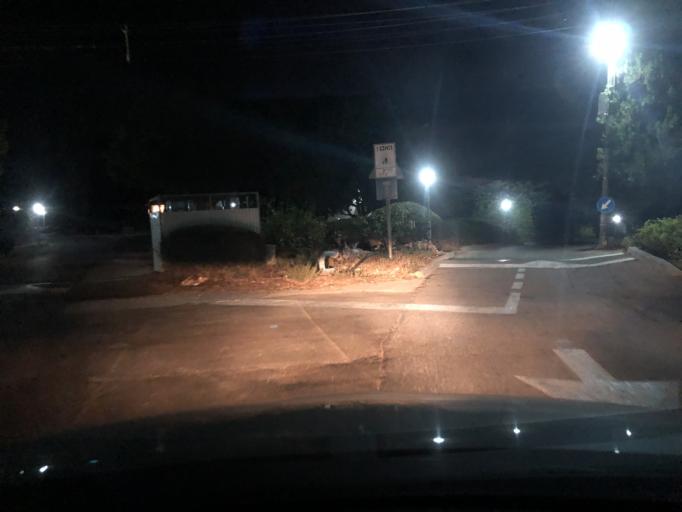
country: IL
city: Nirit
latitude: 32.1369
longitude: 34.9726
